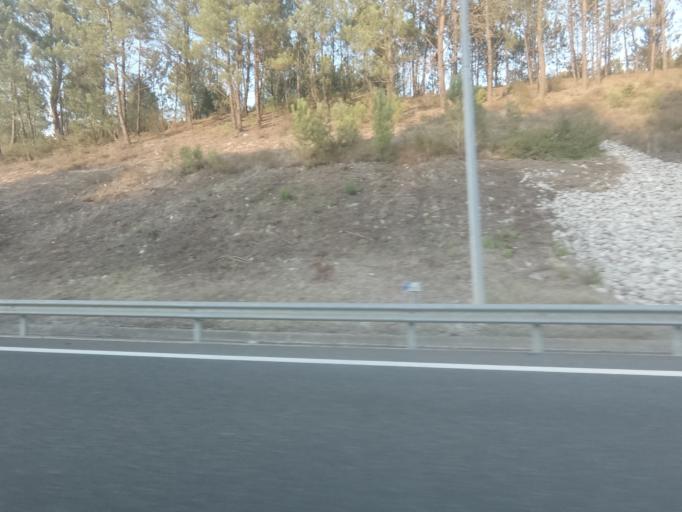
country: PT
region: Leiria
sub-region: Leiria
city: Caranguejeira
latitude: 39.7103
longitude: -8.7089
